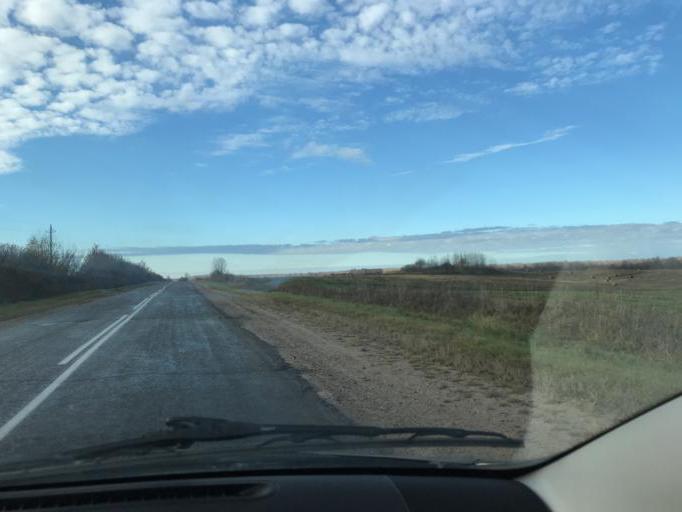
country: BY
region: Vitebsk
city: Haradok
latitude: 55.4120
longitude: 29.7590
